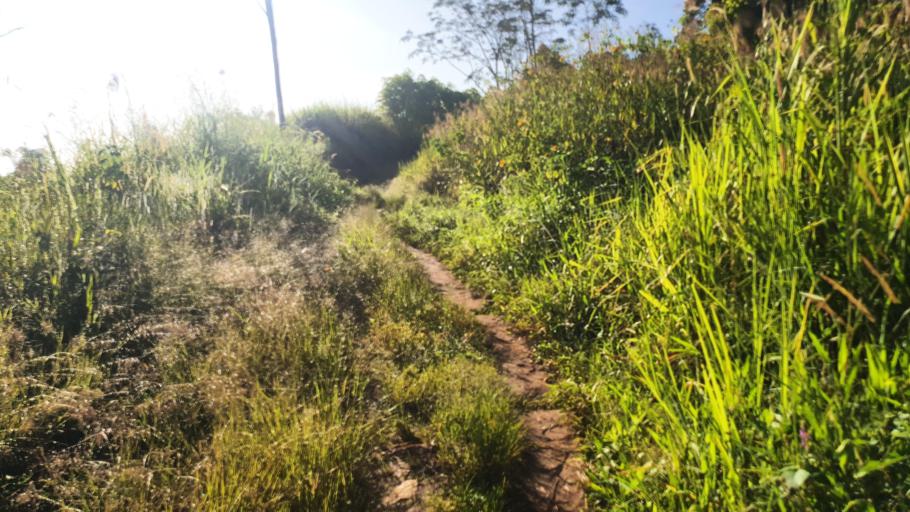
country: PG
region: Western Highlands
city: Rauna
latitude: -5.8002
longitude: 144.3651
